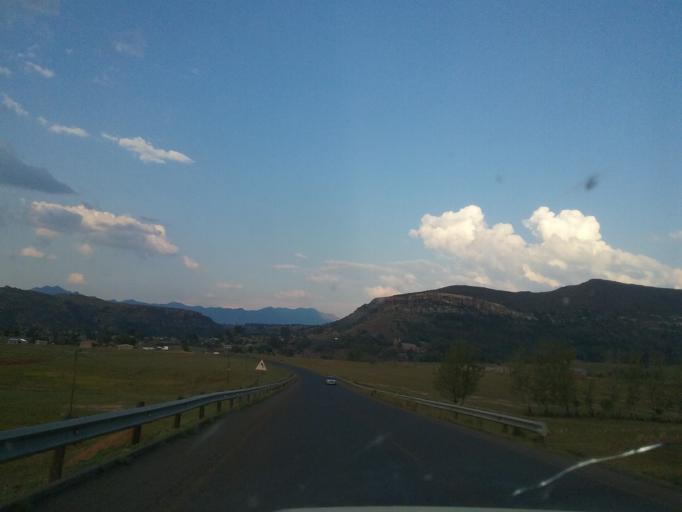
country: LS
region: Quthing
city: Quthing
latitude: -30.3978
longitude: 27.6531
